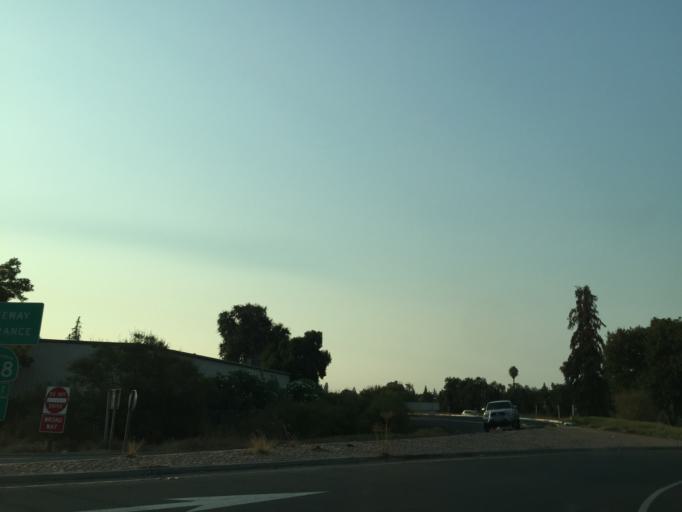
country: US
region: California
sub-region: Tulare County
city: Visalia
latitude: 36.3273
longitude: -119.2760
